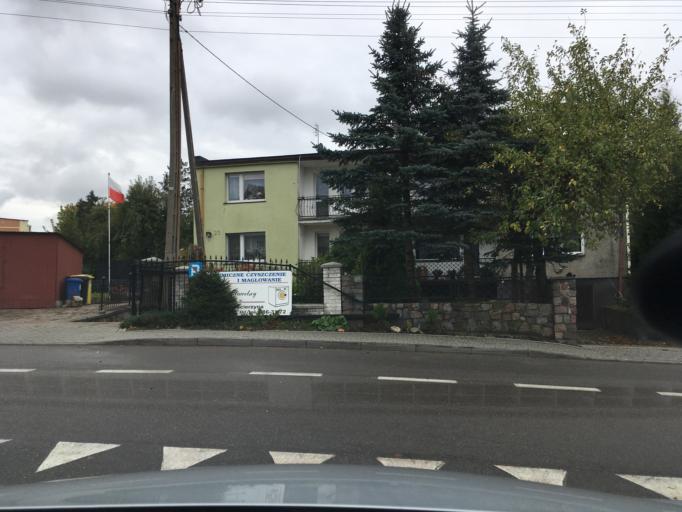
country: PL
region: Pomeranian Voivodeship
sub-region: Powiat koscierski
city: Koscierzyna
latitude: 54.1179
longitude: 17.9898
